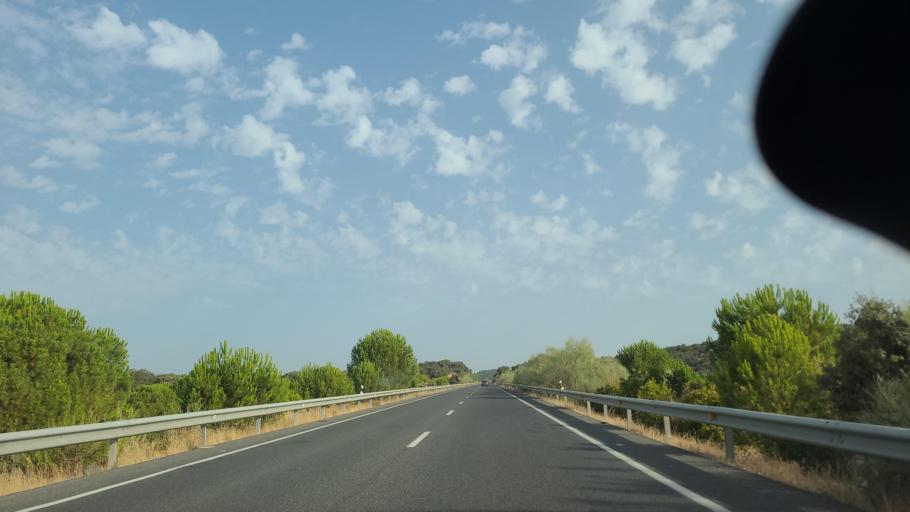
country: ES
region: Andalusia
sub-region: Province of Cordoba
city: Cordoba
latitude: 38.0095
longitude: -4.8034
